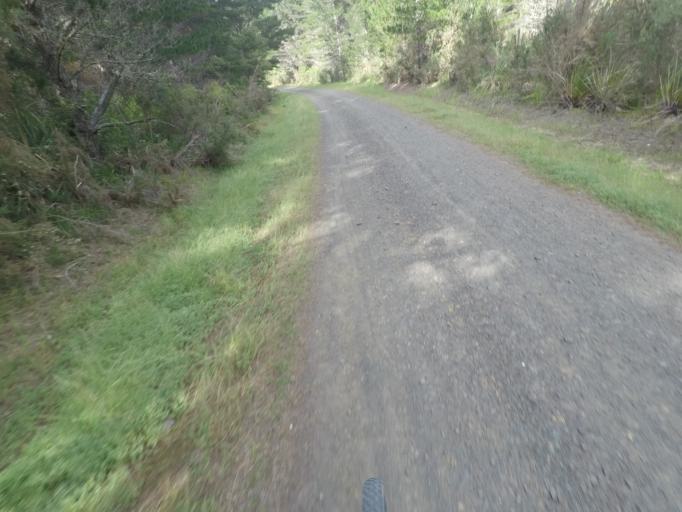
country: NZ
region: Auckland
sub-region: Auckland
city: Muriwai Beach
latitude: -36.7441
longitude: 174.5663
